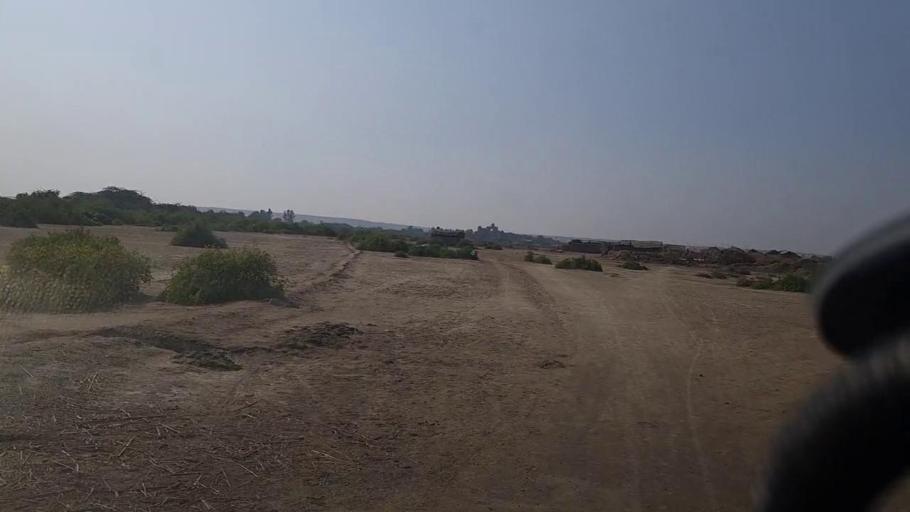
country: PK
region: Sindh
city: Thatta
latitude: 24.6195
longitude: 67.8831
